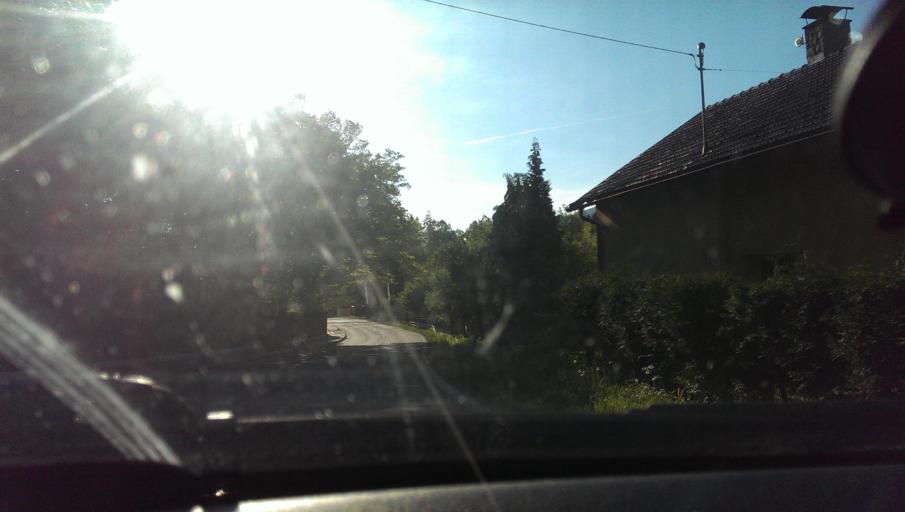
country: CZ
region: Moravskoslezsky
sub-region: Okres Frydek-Mistek
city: Celadna
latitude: 49.5388
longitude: 18.3090
